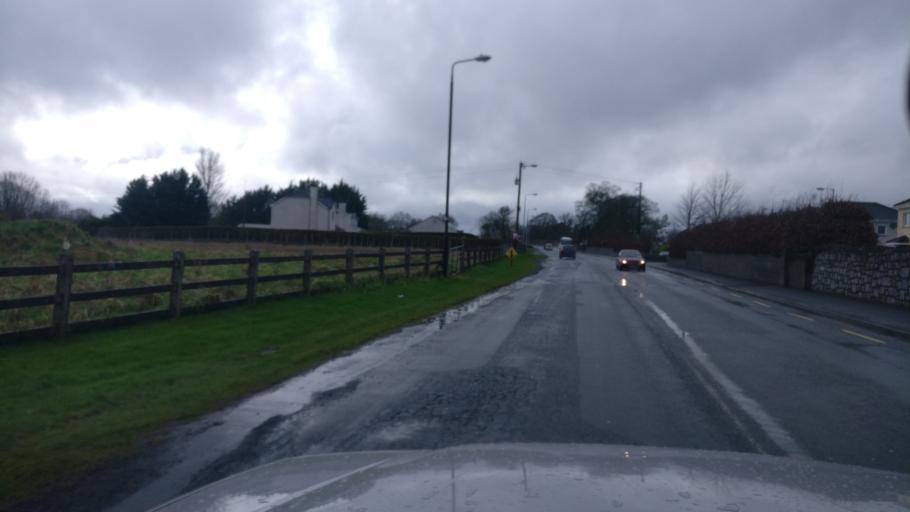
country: IE
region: Leinster
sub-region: An Iarmhi
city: Athlone
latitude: 53.4263
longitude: -8.0112
